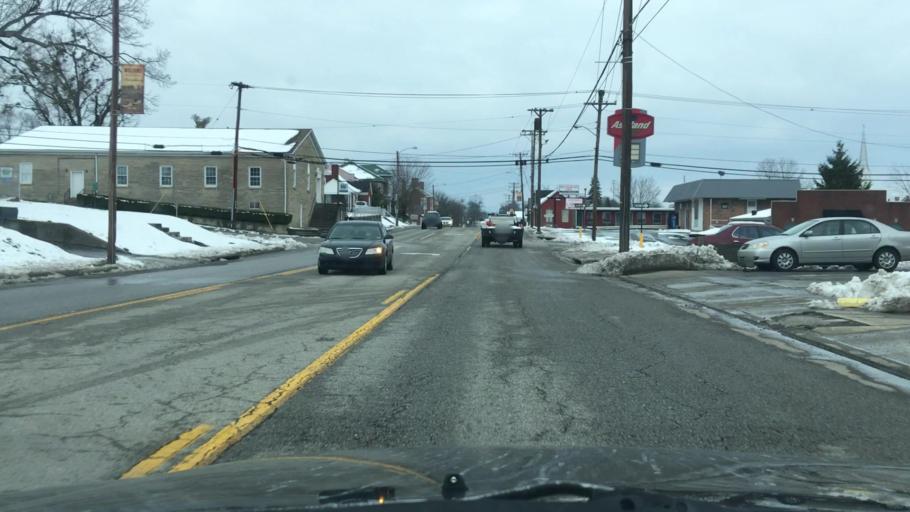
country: US
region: Kentucky
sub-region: Mercer County
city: Harrodsburg
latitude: 37.7597
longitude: -84.8459
